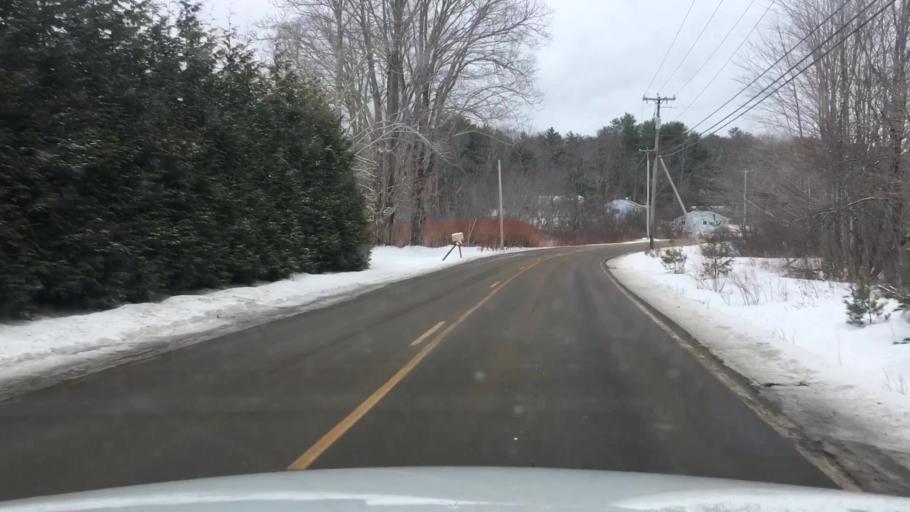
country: US
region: Maine
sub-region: Waldo County
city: Lincolnville
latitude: 44.2847
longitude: -69.0376
